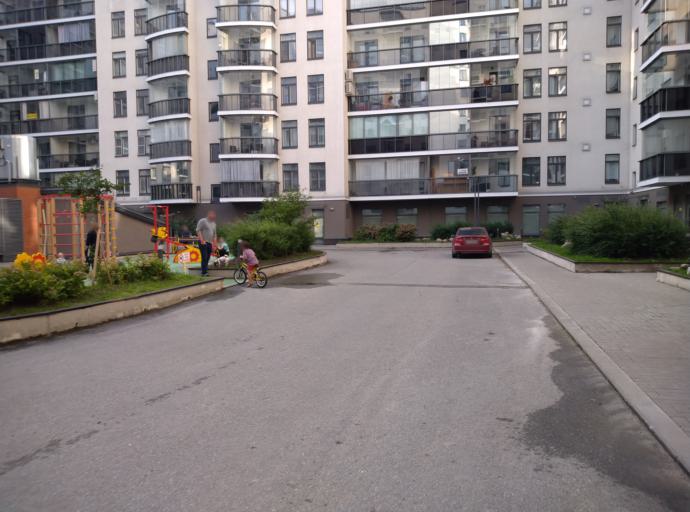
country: RU
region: St.-Petersburg
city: Admiralteisky
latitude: 59.9076
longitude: 30.3133
